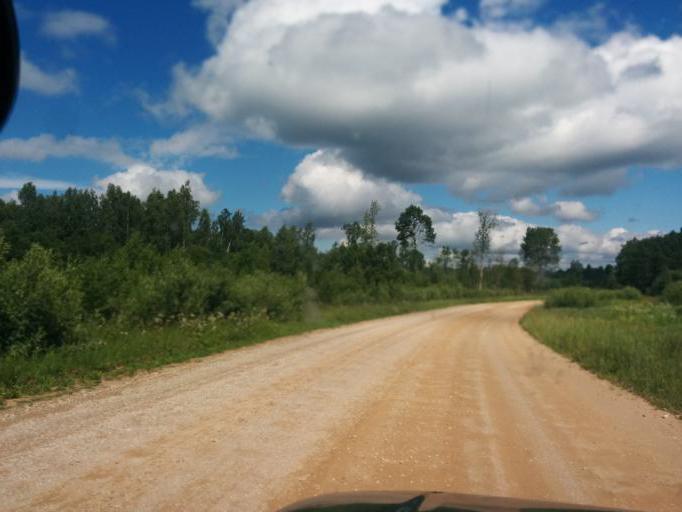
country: LV
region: Vilaka
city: Vilaka
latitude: 57.2758
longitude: 27.4764
